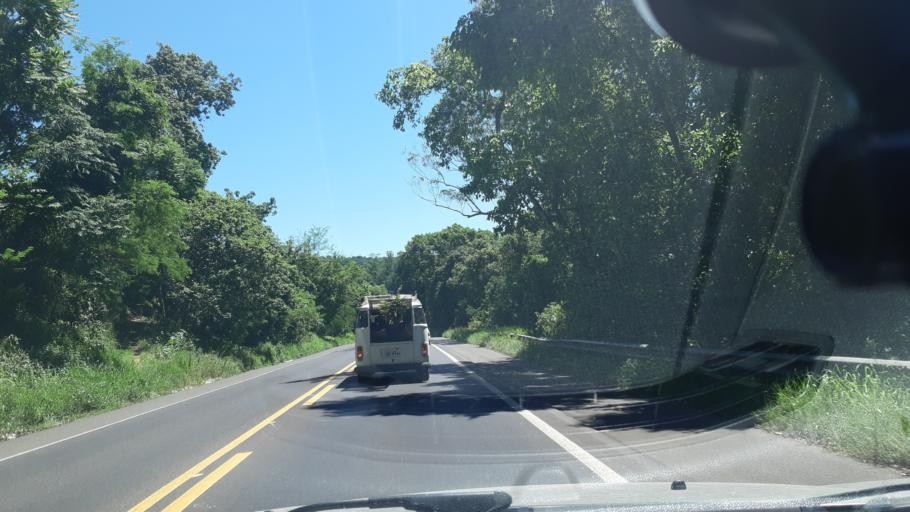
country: BR
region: Rio Grande do Sul
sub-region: Estancia Velha
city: Estancia Velha
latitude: -29.6424
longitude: -51.1427
